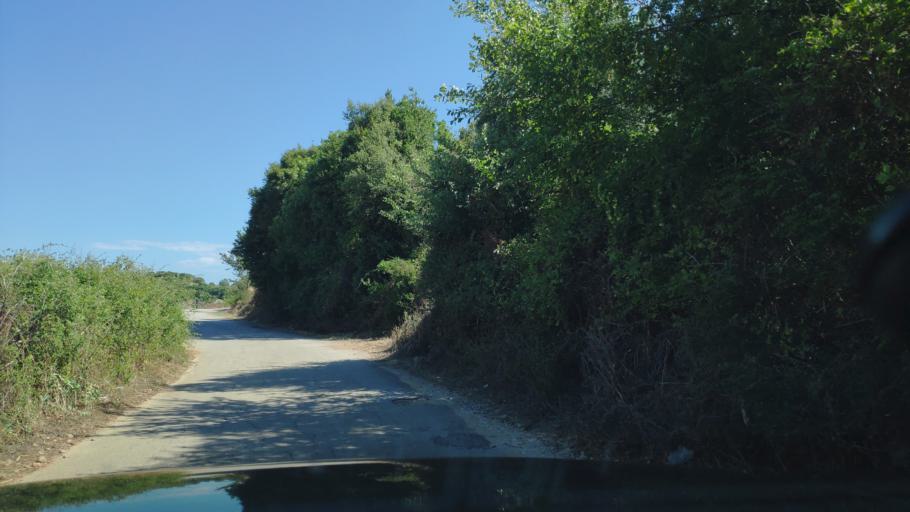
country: GR
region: West Greece
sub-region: Nomos Aitolias kai Akarnanias
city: Katouna
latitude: 38.7964
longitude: 21.1135
